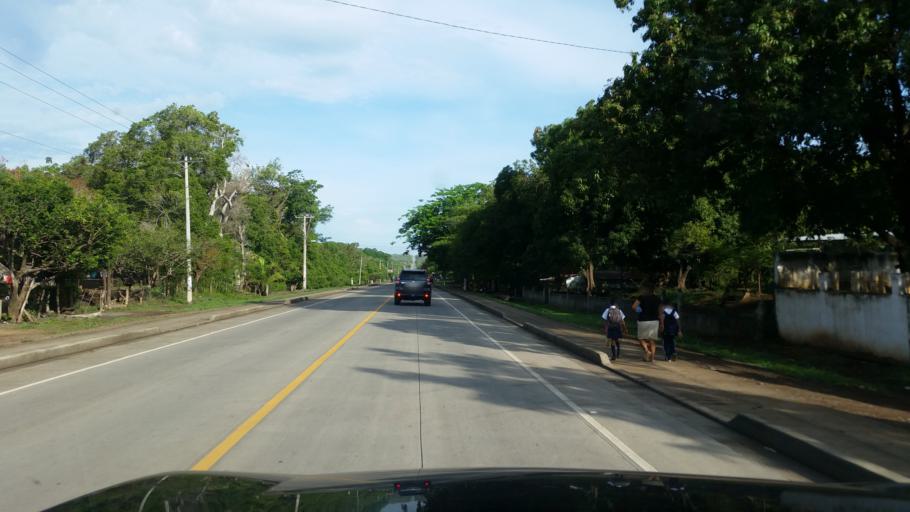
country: NI
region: Managua
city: Carlos Fonseca Amador
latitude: 12.1079
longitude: -86.5912
